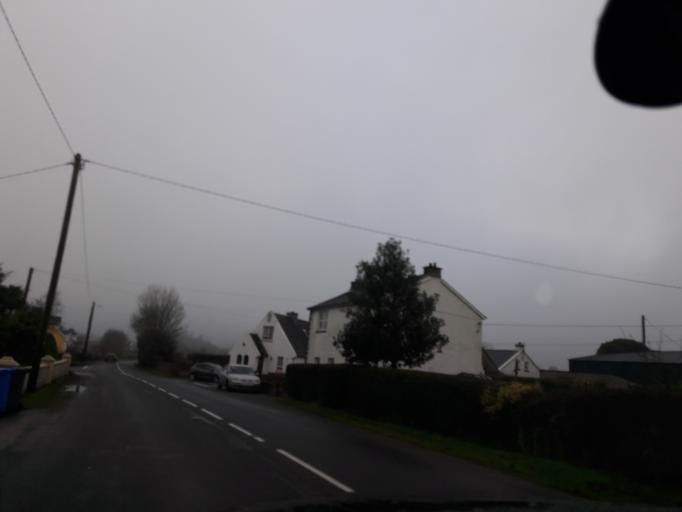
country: IE
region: Ulster
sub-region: County Donegal
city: Ramelton
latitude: 55.0306
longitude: -7.6482
